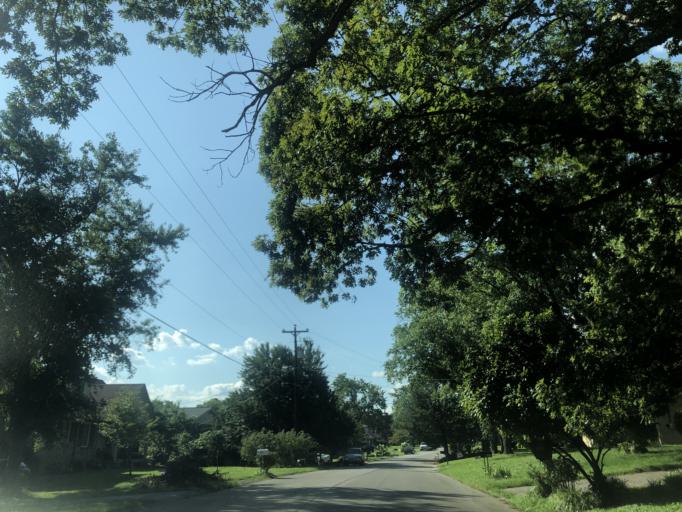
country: US
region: Tennessee
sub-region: Wilson County
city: Green Hill
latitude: 36.2087
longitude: -86.5954
